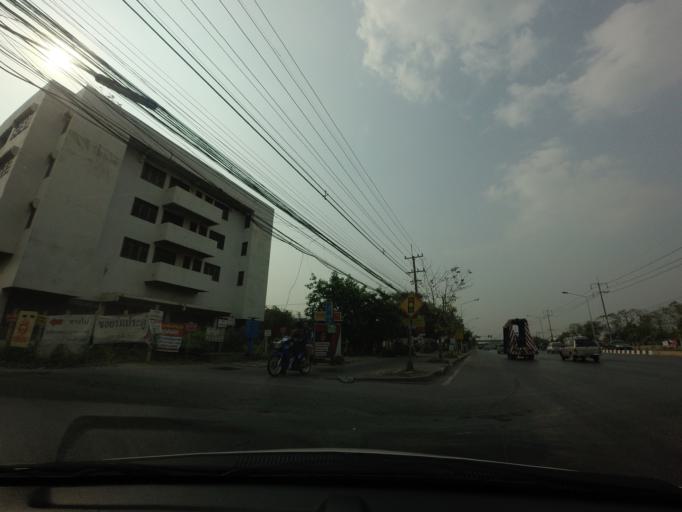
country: TH
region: Bangkok
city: Nong Khaem
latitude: 13.7325
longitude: 100.3298
